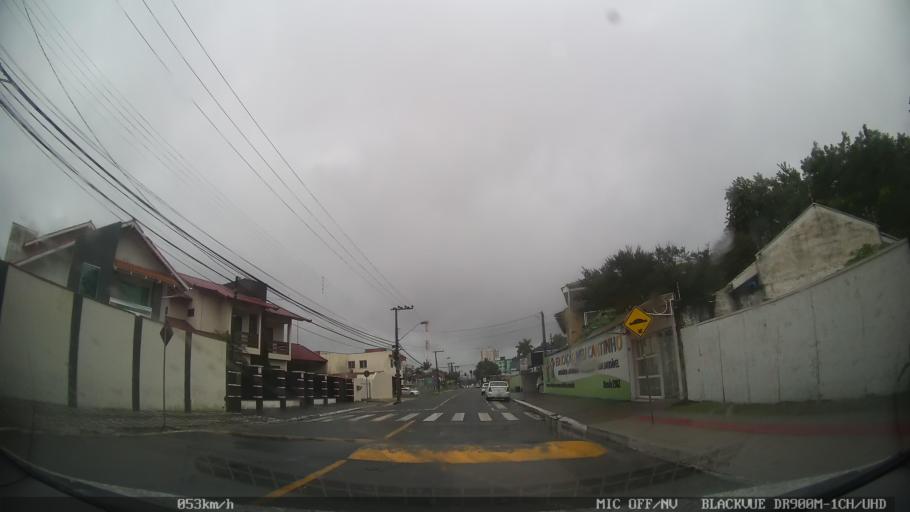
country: BR
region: Santa Catarina
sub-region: Itajai
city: Itajai
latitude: -26.9220
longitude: -48.6785
